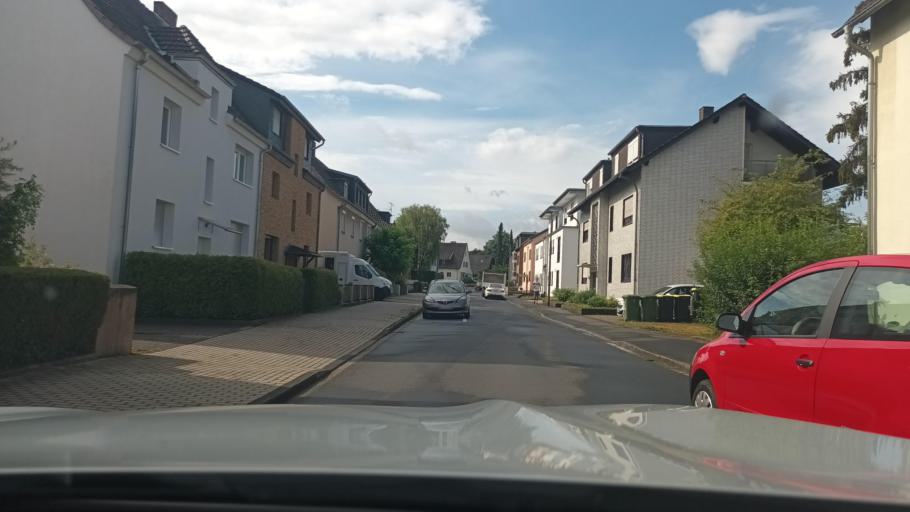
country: DE
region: North Rhine-Westphalia
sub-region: Regierungsbezirk Koln
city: Hennef
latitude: 50.7795
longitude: 7.2822
